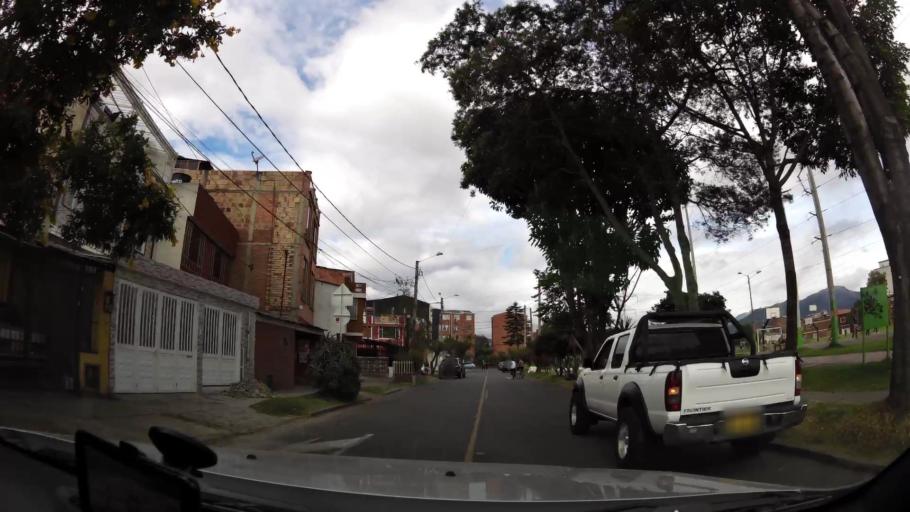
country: CO
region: Bogota D.C.
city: Bogota
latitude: 4.6089
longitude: -74.1322
